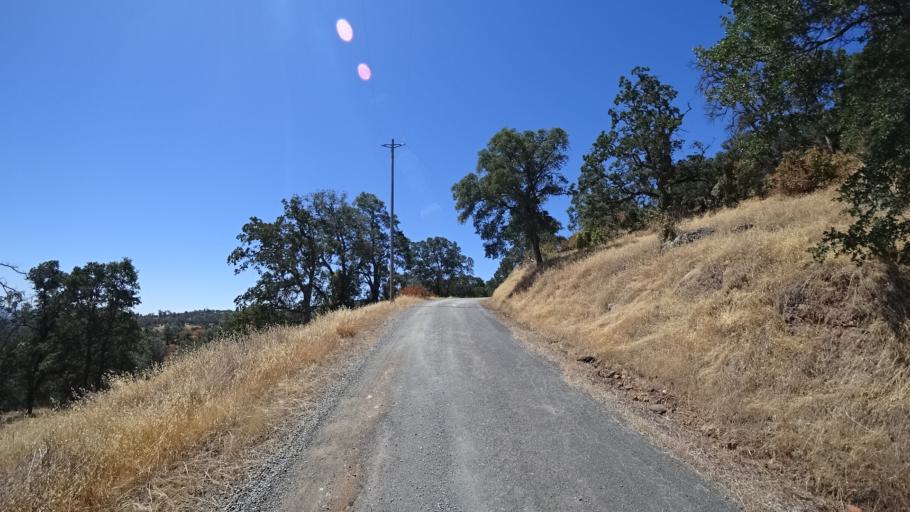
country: US
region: California
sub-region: Calaveras County
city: Copperopolis
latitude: 37.9558
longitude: -120.6994
